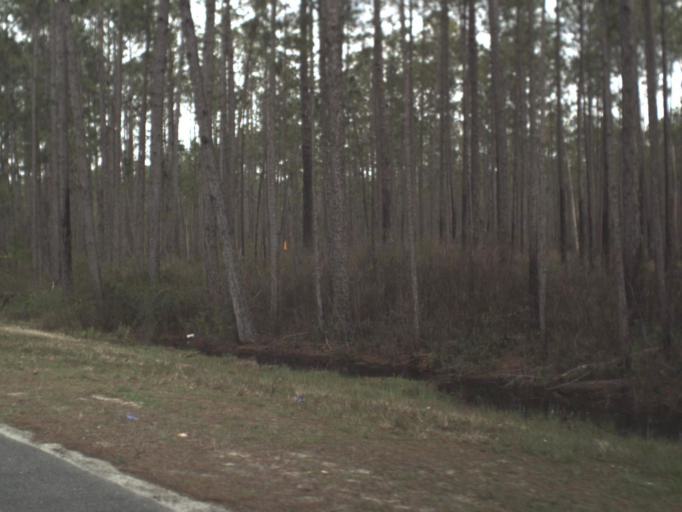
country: US
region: Florida
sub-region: Gadsden County
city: Midway
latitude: 30.3887
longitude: -84.6067
